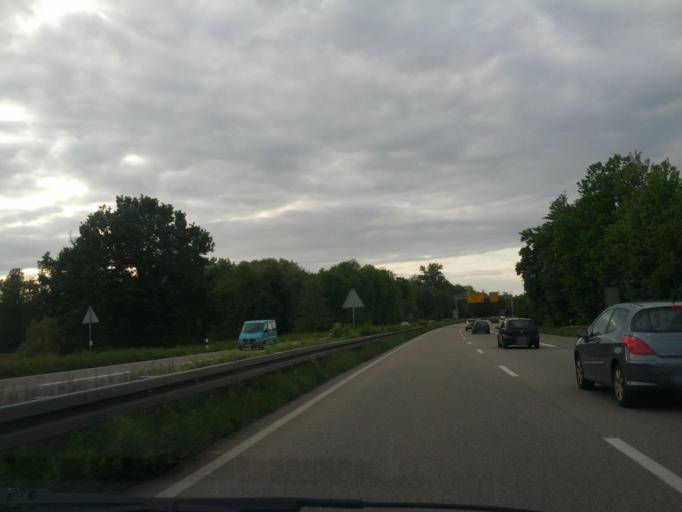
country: DE
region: Baden-Wuerttemberg
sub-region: Freiburg Region
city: Gundelfingen
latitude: 48.0398
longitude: 7.8589
